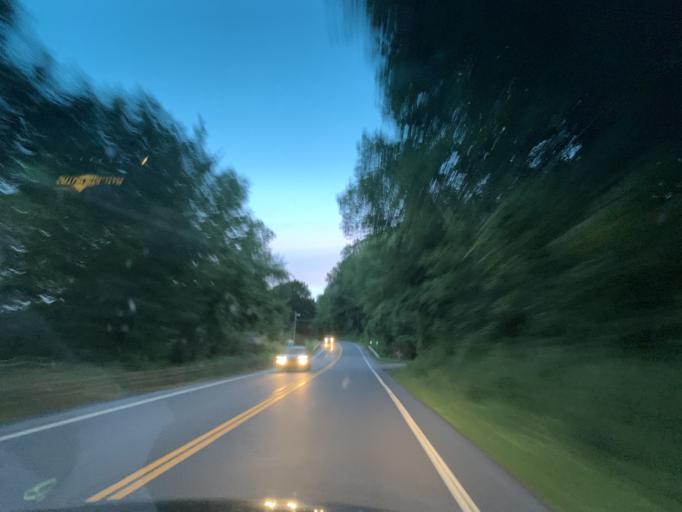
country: US
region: New York
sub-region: Chenango County
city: New Berlin
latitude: 42.6120
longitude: -75.3388
